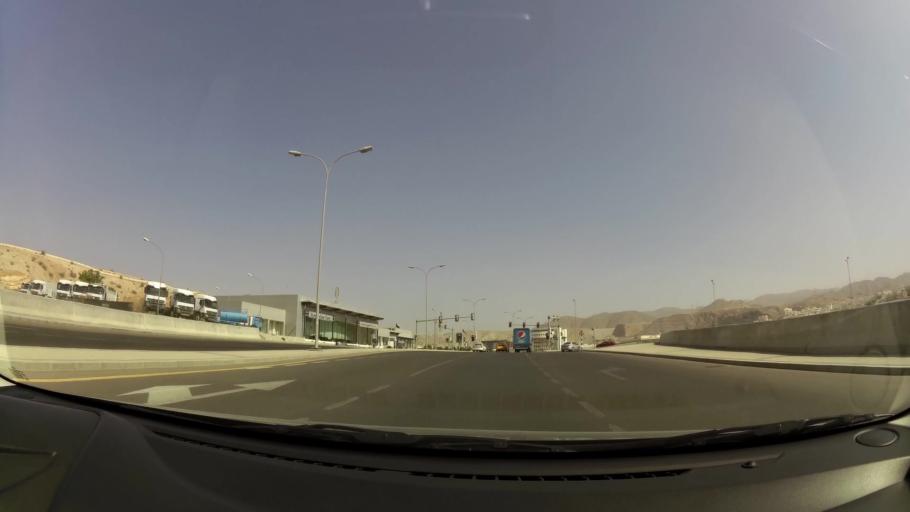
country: OM
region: Muhafazat Masqat
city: Muscat
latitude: 23.6115
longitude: 58.4988
